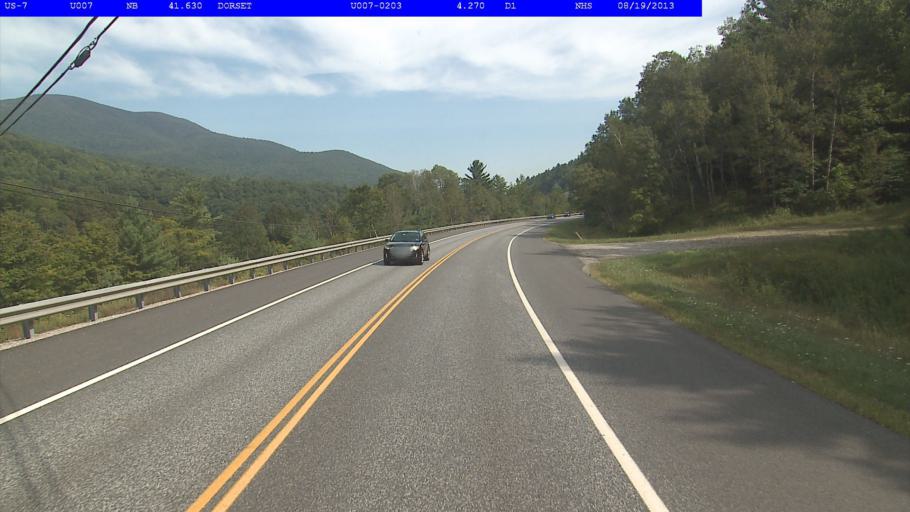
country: US
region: Vermont
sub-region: Bennington County
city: Manchester Center
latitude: 43.2706
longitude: -73.0065
